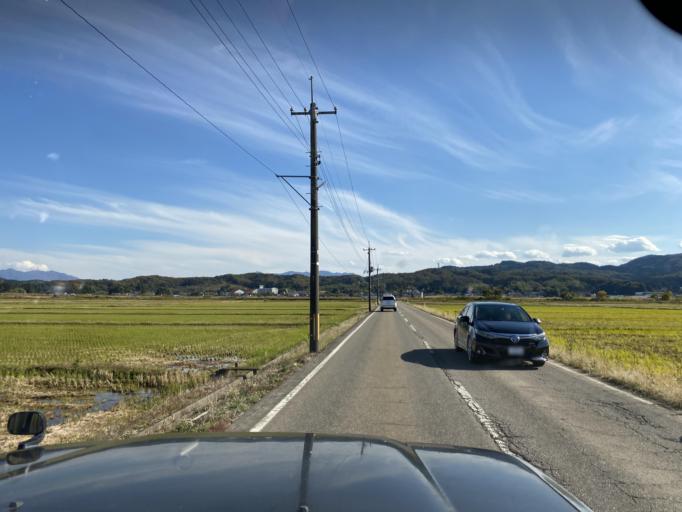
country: JP
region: Niigata
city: Niitsu-honcho
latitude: 37.7580
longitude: 139.0880
